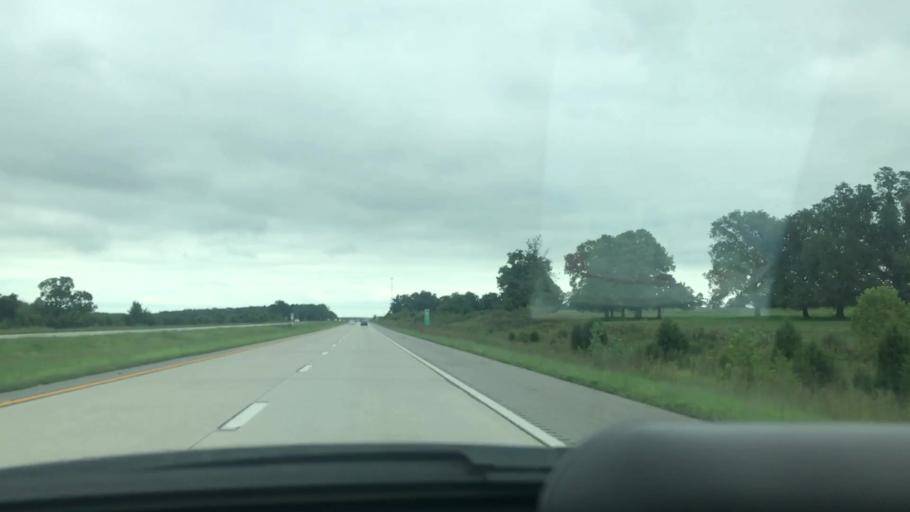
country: US
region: Missouri
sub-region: Greene County
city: Fair Grove
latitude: 37.4944
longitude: -93.1390
